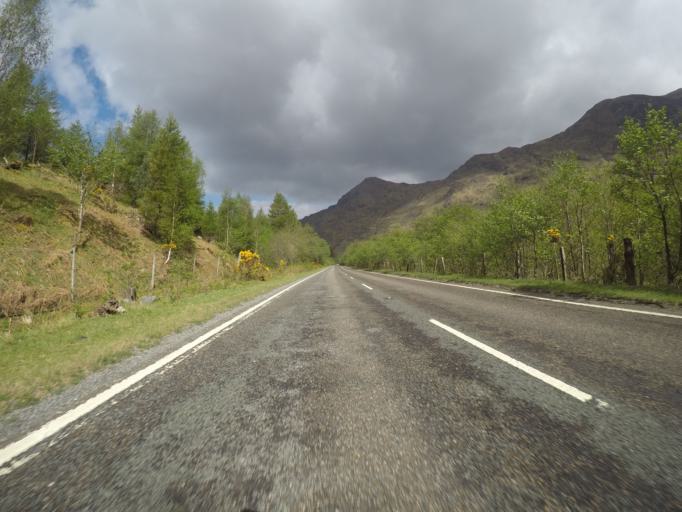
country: GB
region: Scotland
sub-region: Highland
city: Fort William
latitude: 57.1989
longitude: -5.3926
